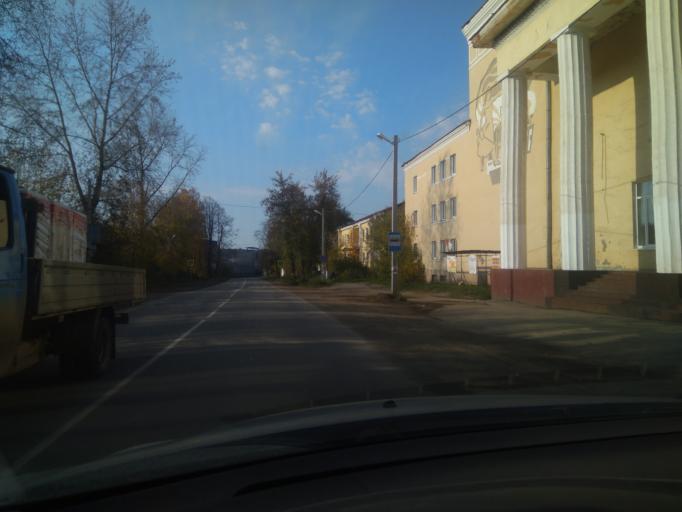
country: RU
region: Sverdlovsk
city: Nizhniye Sergi
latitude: 56.6678
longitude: 59.3171
